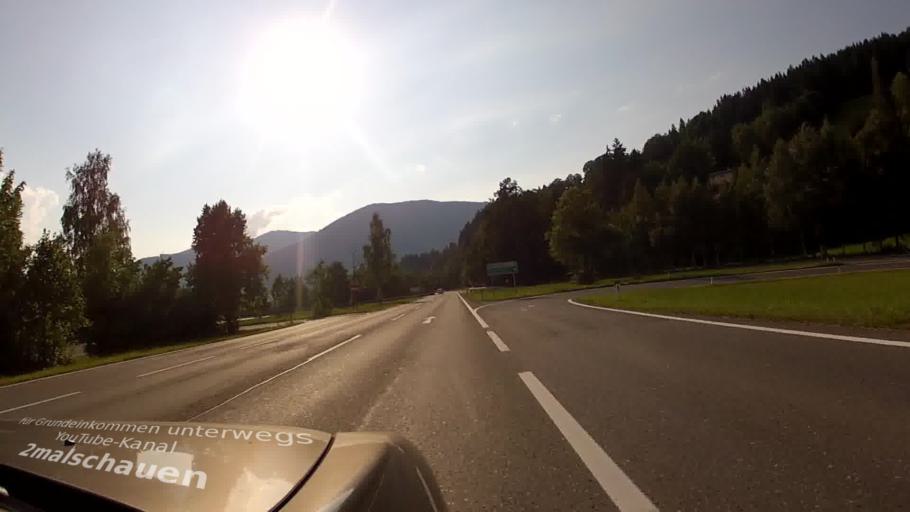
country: AT
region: Salzburg
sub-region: Politischer Bezirk Sankt Johann im Pongau
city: Altenmarkt im Pongau
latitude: 47.3841
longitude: 13.4296
